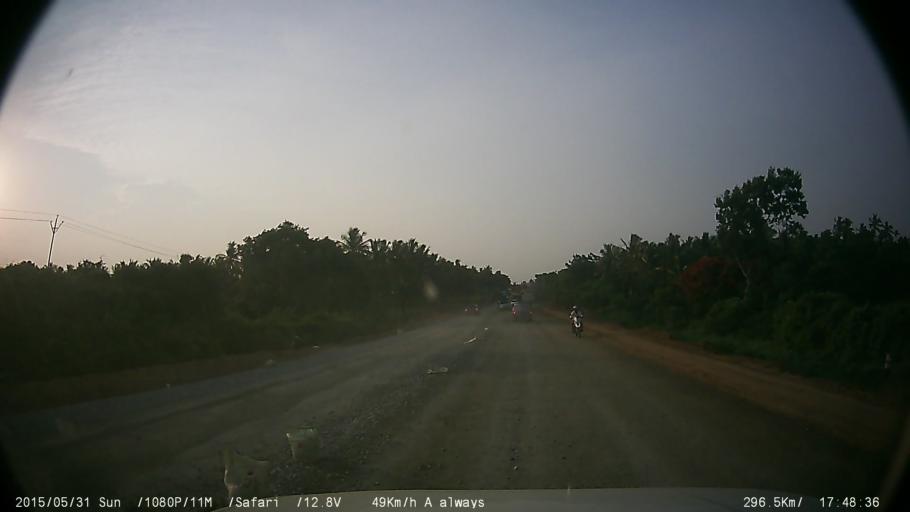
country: IN
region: Karnataka
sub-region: Mysore
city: Nanjangud
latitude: 11.9674
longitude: 76.6702
